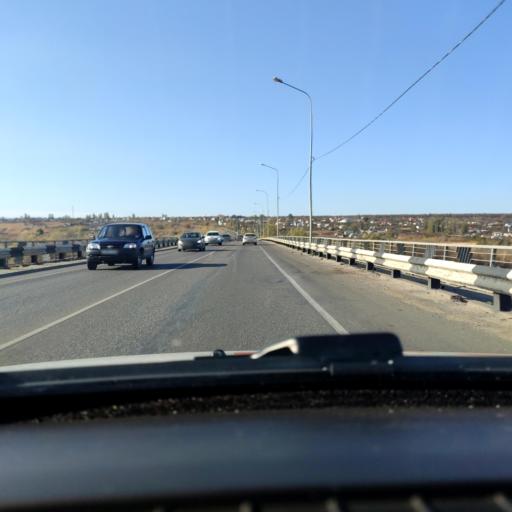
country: RU
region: Voronezj
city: Pridonskoy
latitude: 51.7233
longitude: 39.0634
